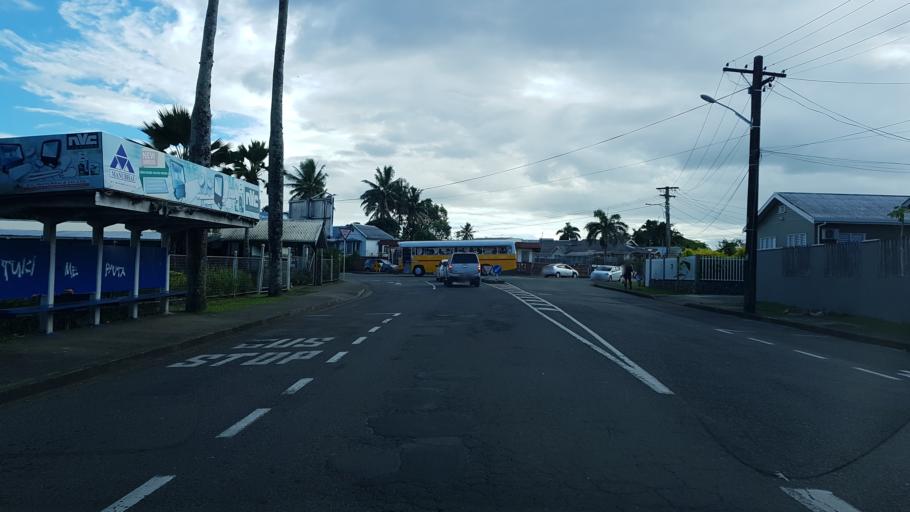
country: FJ
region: Central
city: Suva
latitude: -18.1463
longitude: 178.4319
